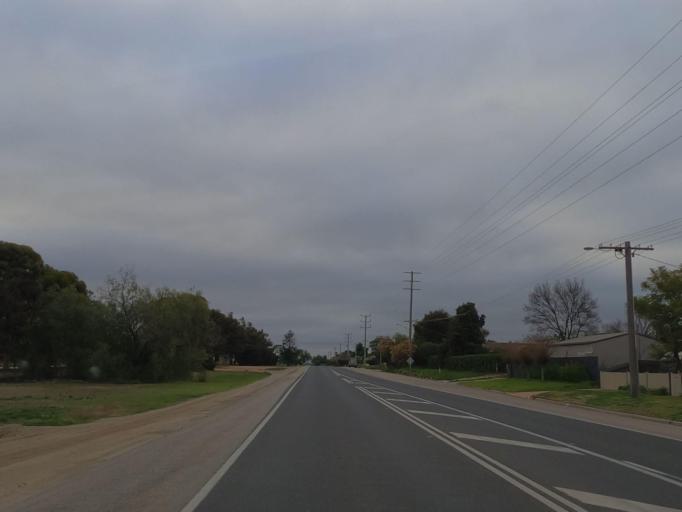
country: AU
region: Victoria
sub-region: Swan Hill
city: Swan Hill
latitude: -35.4611
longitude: 143.6338
